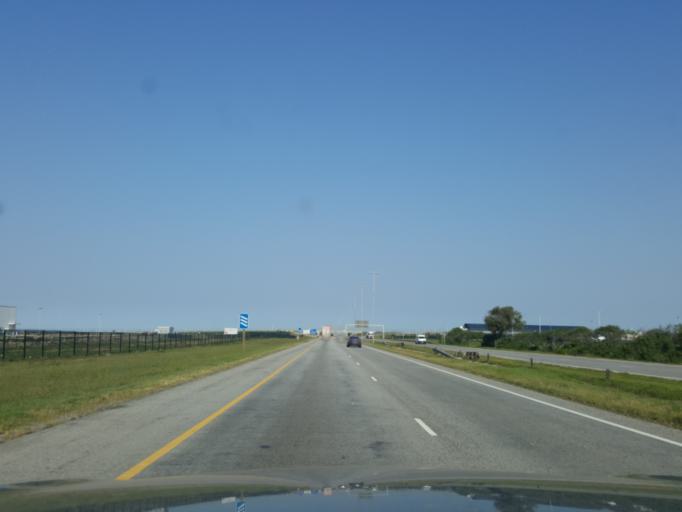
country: ZA
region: Eastern Cape
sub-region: Nelson Mandela Bay Metropolitan Municipality
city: Port Elizabeth
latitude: -33.8152
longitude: 25.6503
